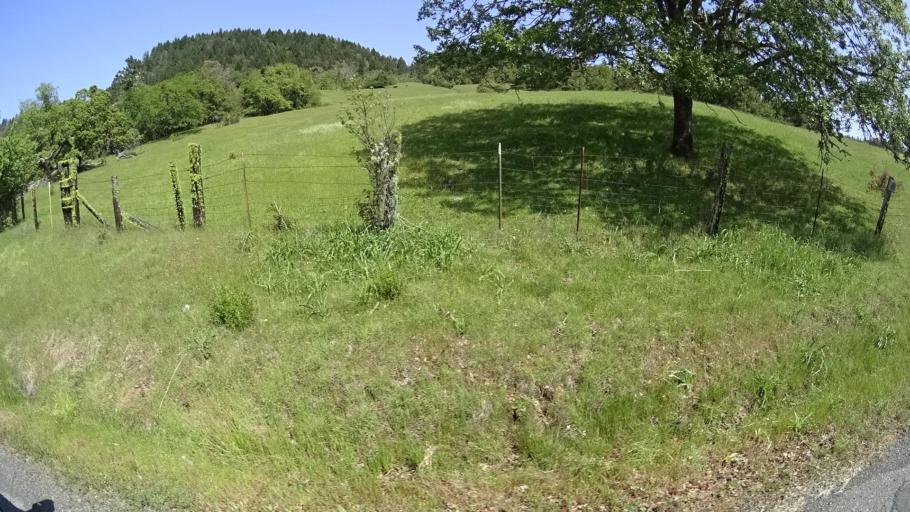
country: US
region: California
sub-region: Humboldt County
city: Redway
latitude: 40.2554
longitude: -123.6246
